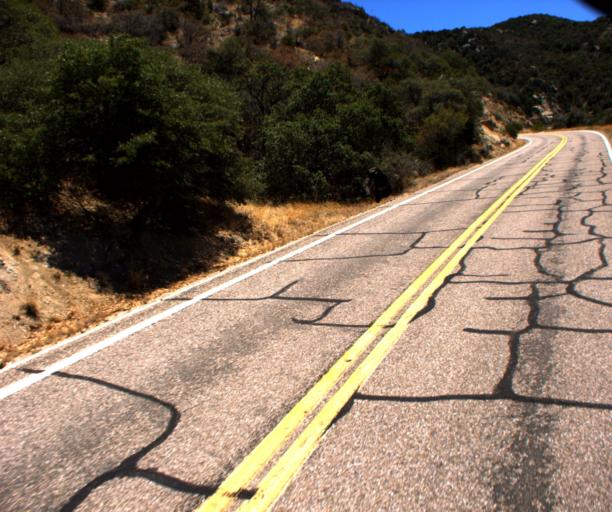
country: US
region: Arizona
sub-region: Pima County
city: Sells
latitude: 31.9675
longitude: -111.6206
